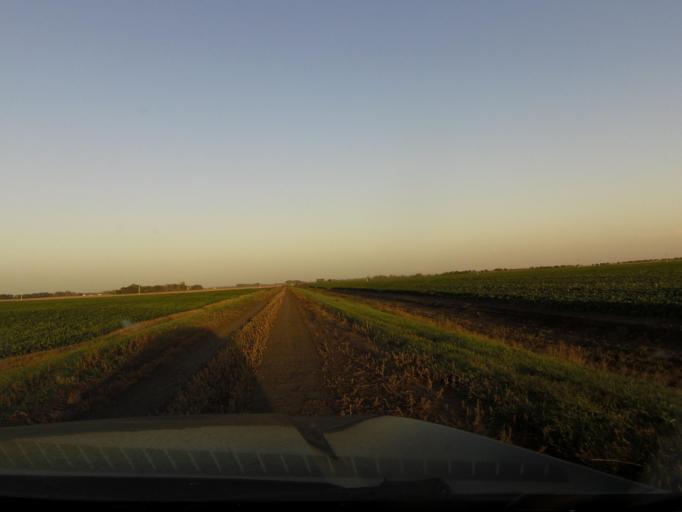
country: US
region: North Dakota
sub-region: Walsh County
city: Grafton
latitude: 48.3831
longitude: -97.2388
